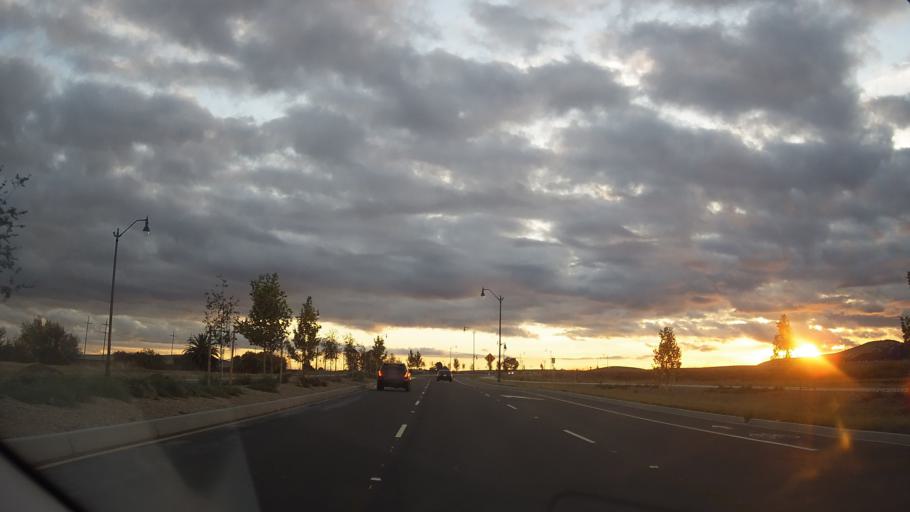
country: US
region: California
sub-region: Solano County
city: Vacaville
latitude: 38.3200
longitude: -121.9375
